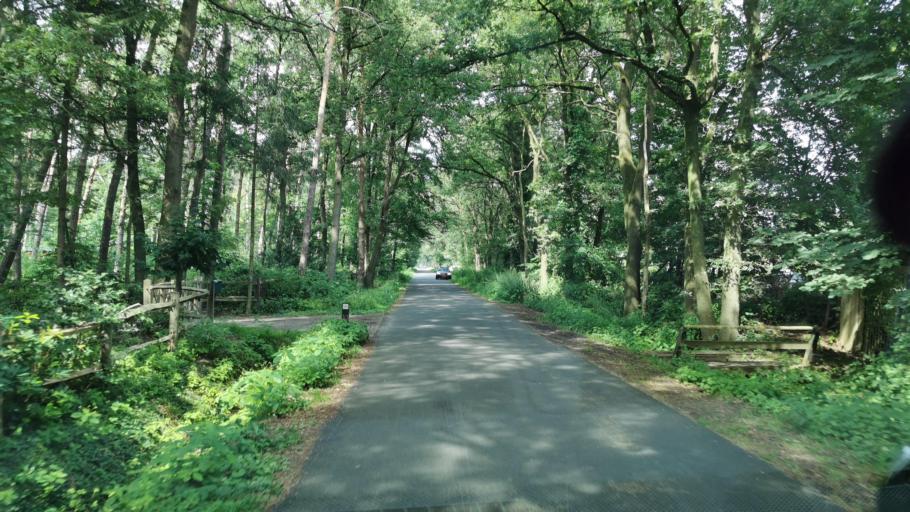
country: NL
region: Overijssel
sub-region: Gemeente Enschede
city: Enschede
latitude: 52.1682
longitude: 6.8682
